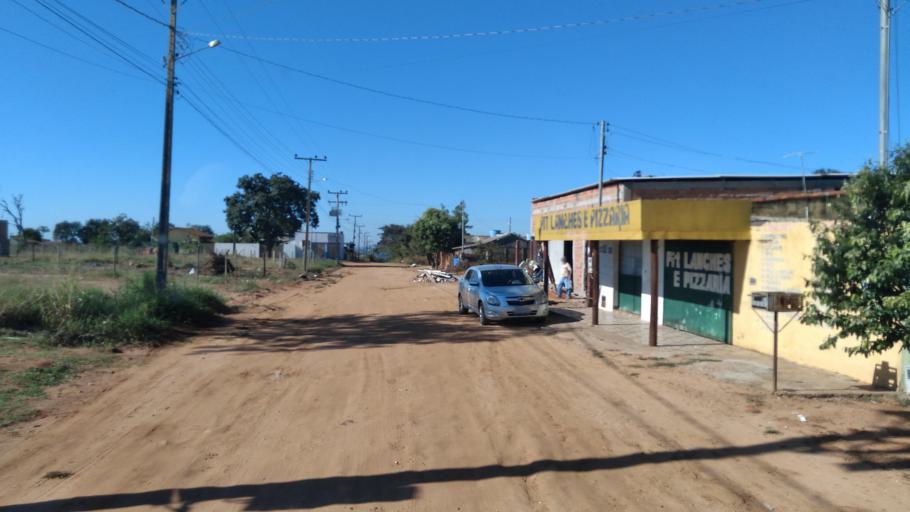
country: BR
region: Goias
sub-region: Mineiros
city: Mineiros
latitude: -17.5899
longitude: -52.5567
